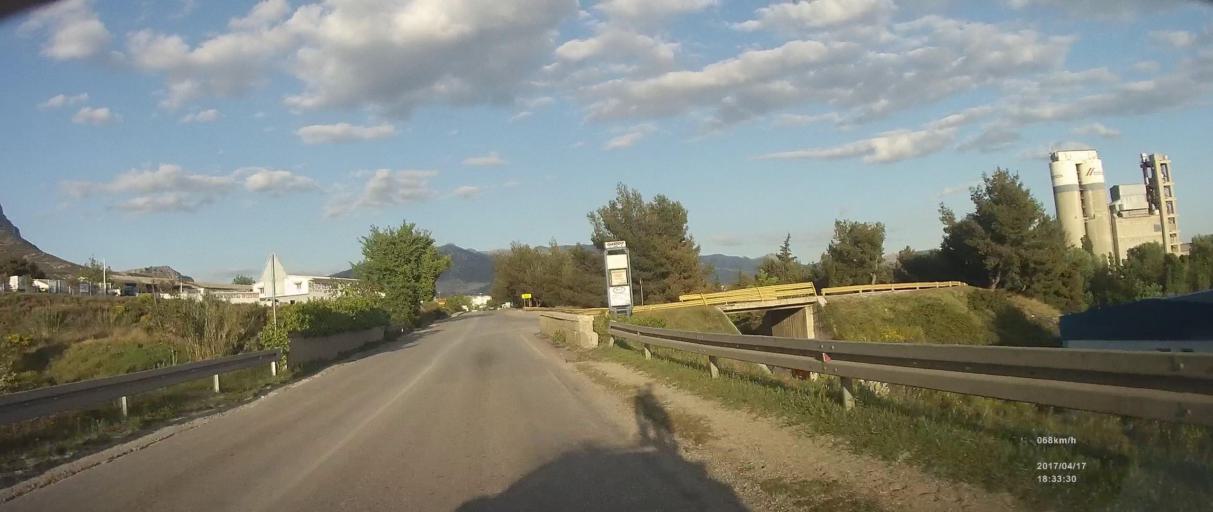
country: HR
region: Splitsko-Dalmatinska
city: Vranjic
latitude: 43.5413
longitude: 16.4606
